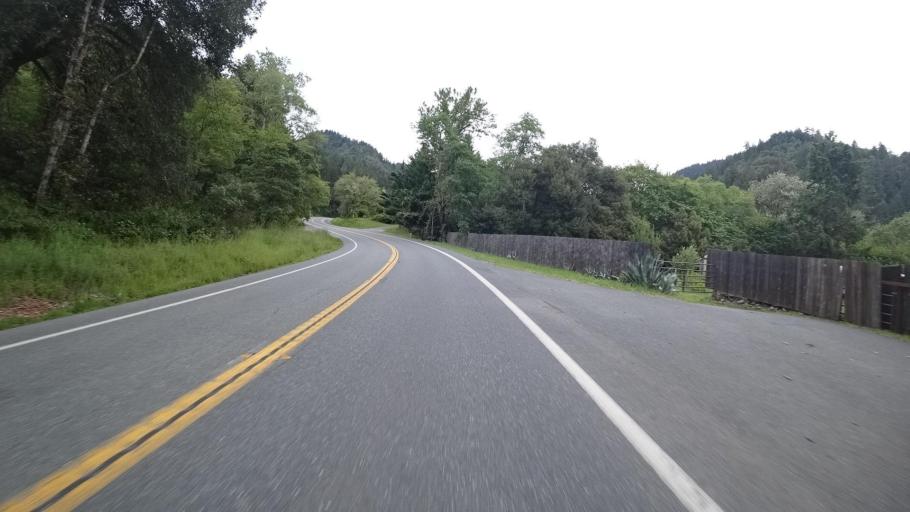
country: US
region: California
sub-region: Humboldt County
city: Willow Creek
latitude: 40.9809
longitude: -123.6397
